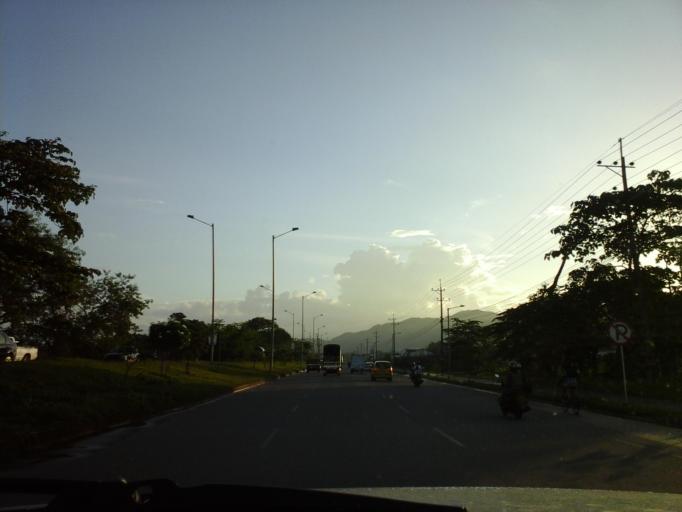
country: CO
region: Meta
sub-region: Villavicencio
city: Villavicencio
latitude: 4.1170
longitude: -73.6251
